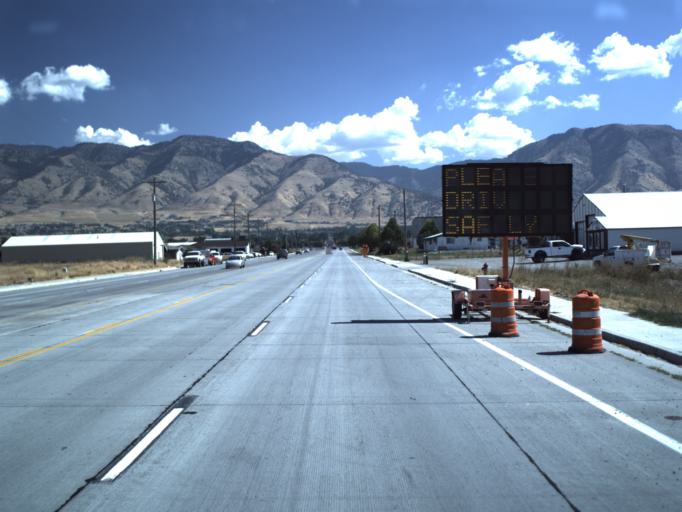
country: US
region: Utah
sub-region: Cache County
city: Hyde Park
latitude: 41.7778
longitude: -111.8453
